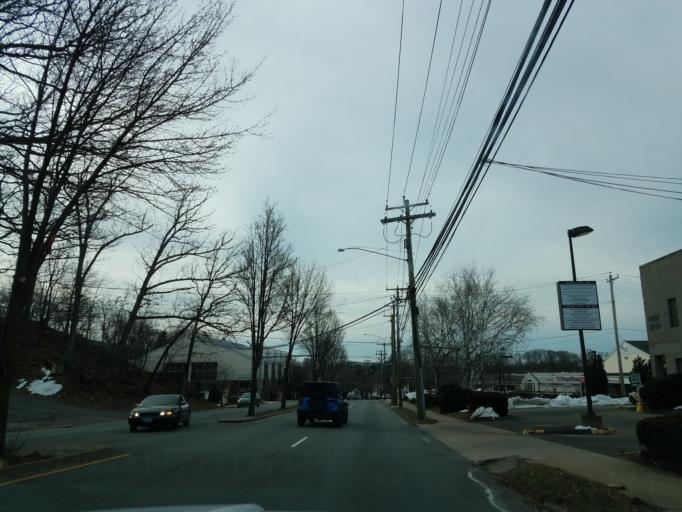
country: US
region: Connecticut
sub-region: Fairfield County
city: Trumbull
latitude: 41.2231
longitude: -73.2182
